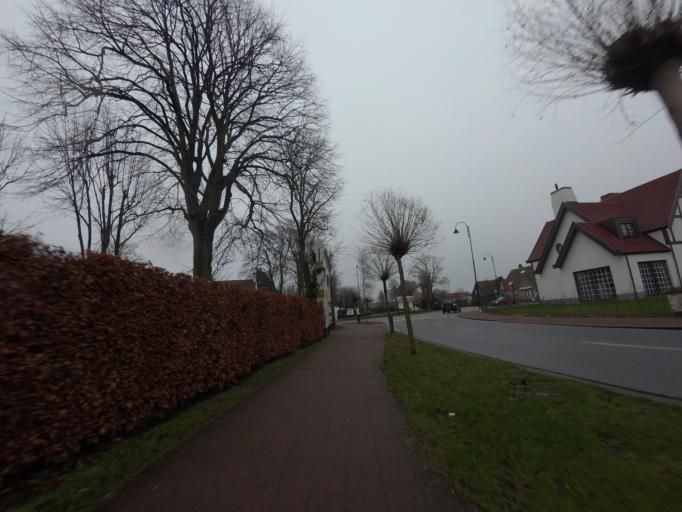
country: BE
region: Flanders
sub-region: Provincie West-Vlaanderen
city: Knokke-Heist
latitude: 51.3254
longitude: 3.3001
